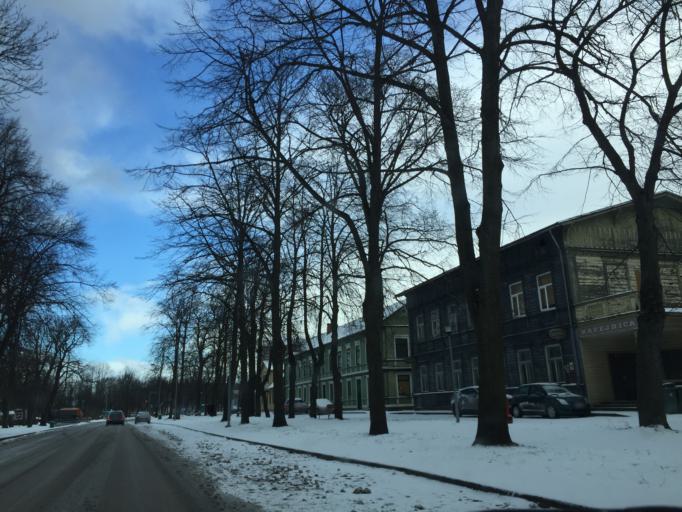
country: LV
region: Ventspils
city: Ventspils
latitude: 57.3903
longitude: 21.5643
